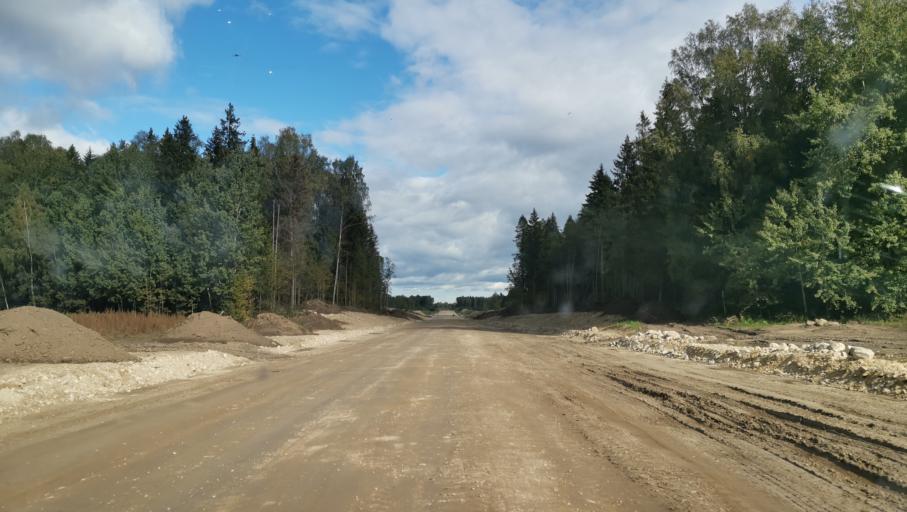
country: EE
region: Harju
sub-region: Nissi vald
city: Riisipere
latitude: 59.1387
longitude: 24.4873
